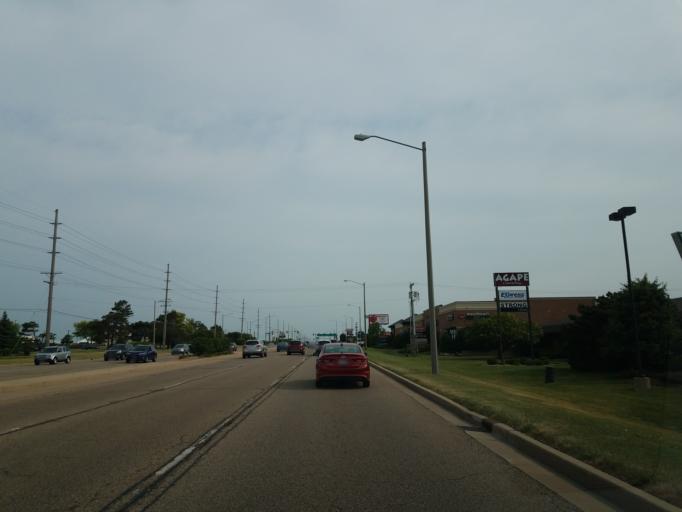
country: US
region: Illinois
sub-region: McLean County
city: Bloomington
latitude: 40.4812
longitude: -88.9525
